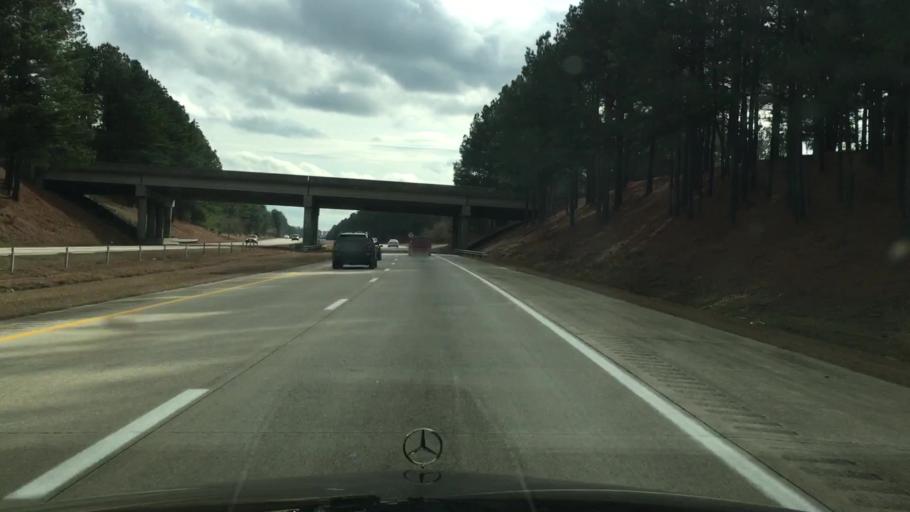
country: US
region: North Carolina
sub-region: Johnston County
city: Benson
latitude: 35.4237
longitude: -78.5306
